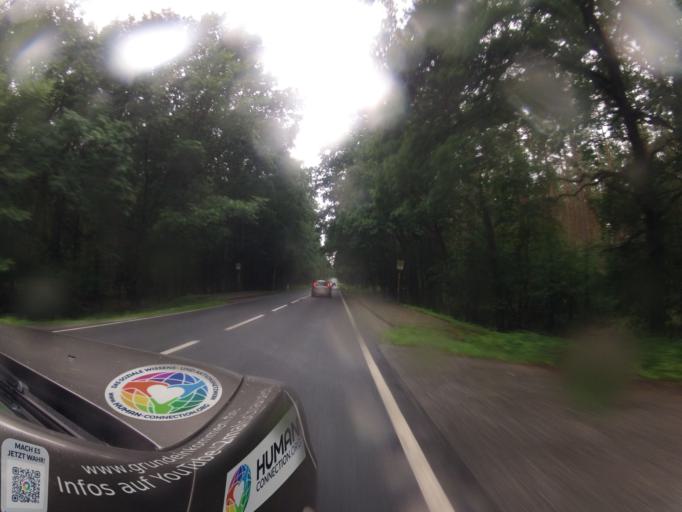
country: DE
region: Mecklenburg-Vorpommern
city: Usedom
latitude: 53.9020
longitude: 13.9943
